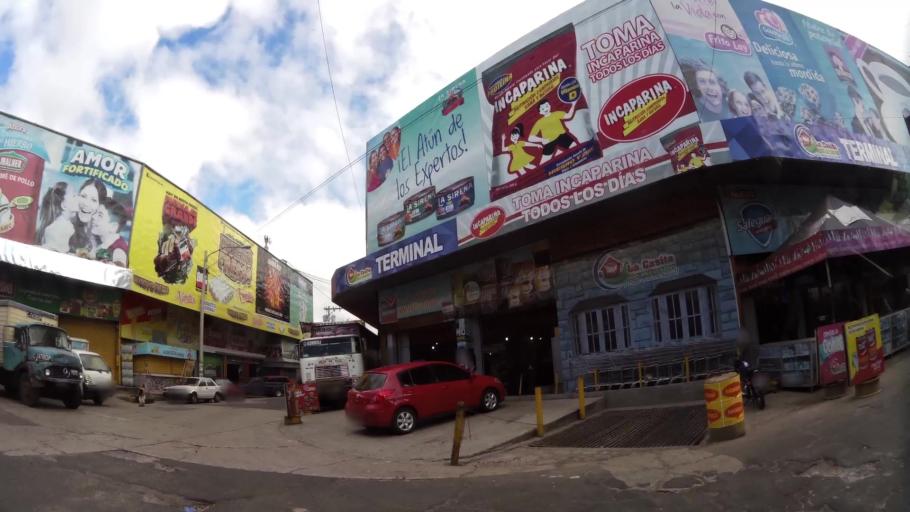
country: GT
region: Guatemala
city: Guatemala City
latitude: 14.6184
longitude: -90.5189
